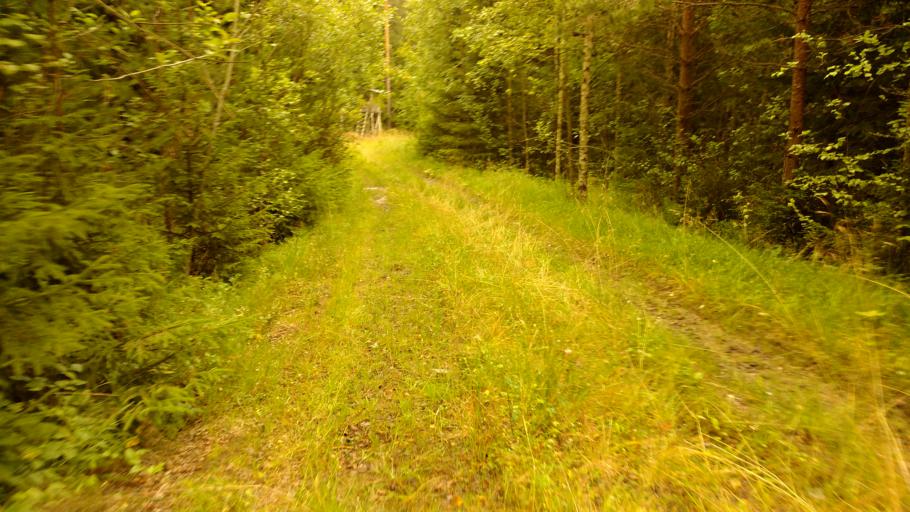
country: FI
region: Varsinais-Suomi
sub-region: Salo
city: Pertteli
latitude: 60.4078
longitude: 23.2322
